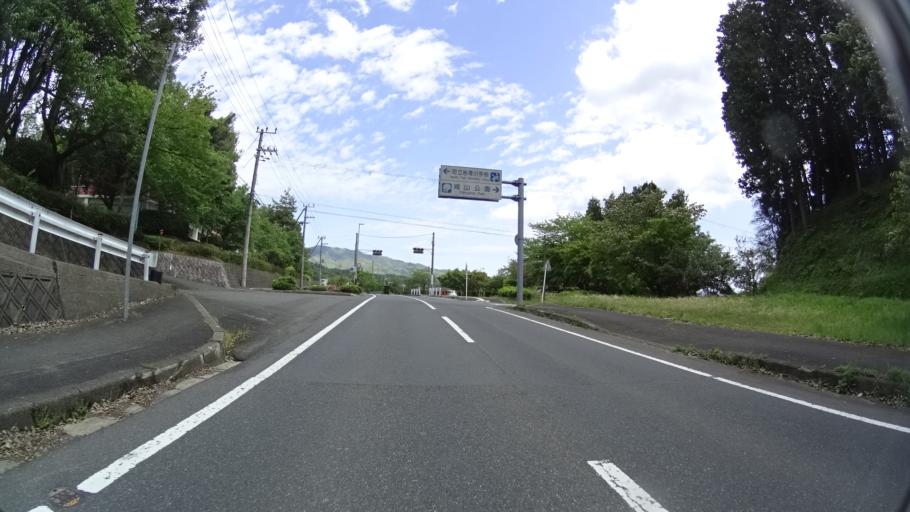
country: JP
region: Kyoto
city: Miyazu
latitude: 35.5655
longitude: 135.1462
